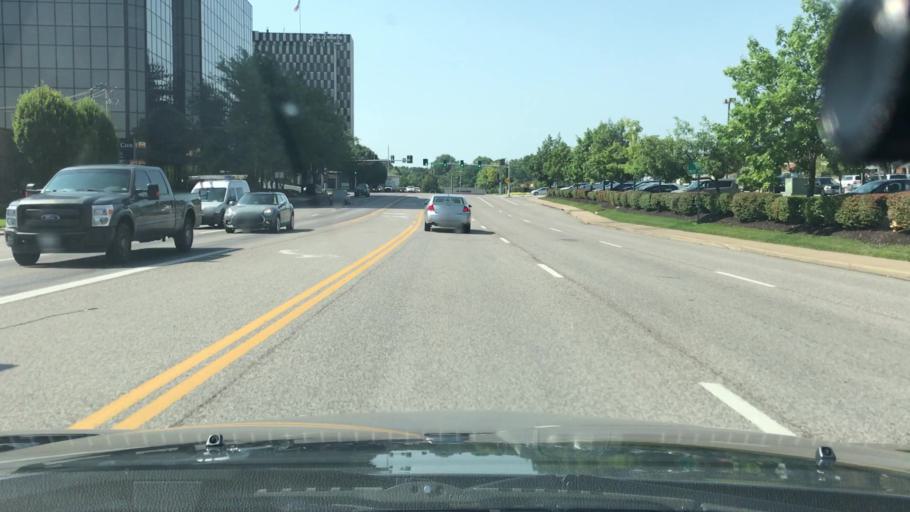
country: US
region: Missouri
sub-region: Saint Louis County
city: Brentwood
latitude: 38.6279
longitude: -90.3465
